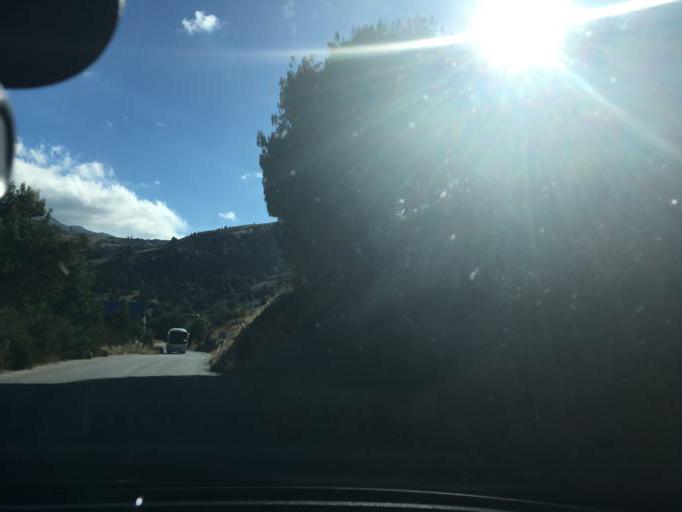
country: CO
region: Boyaca
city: Pesca
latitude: 5.5166
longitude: -72.9753
